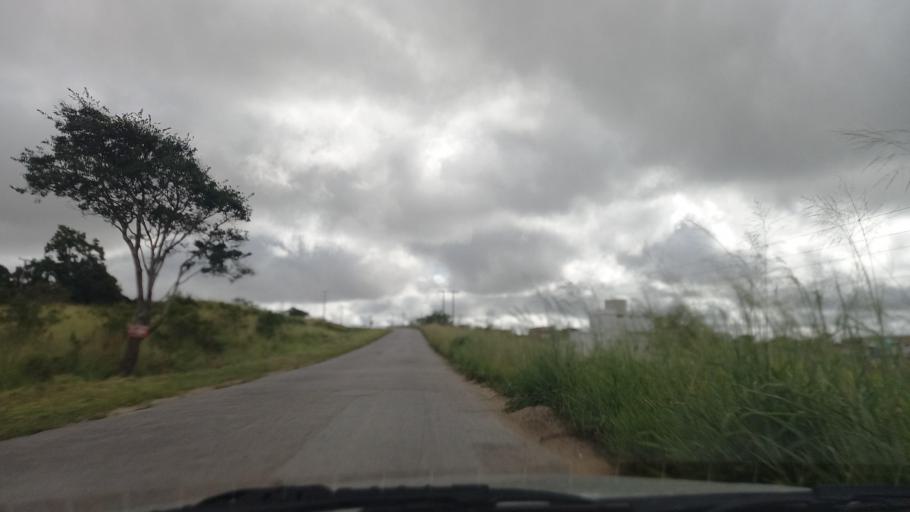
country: BR
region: Pernambuco
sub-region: Caruaru
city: Caruaru
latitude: -8.3275
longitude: -35.9829
